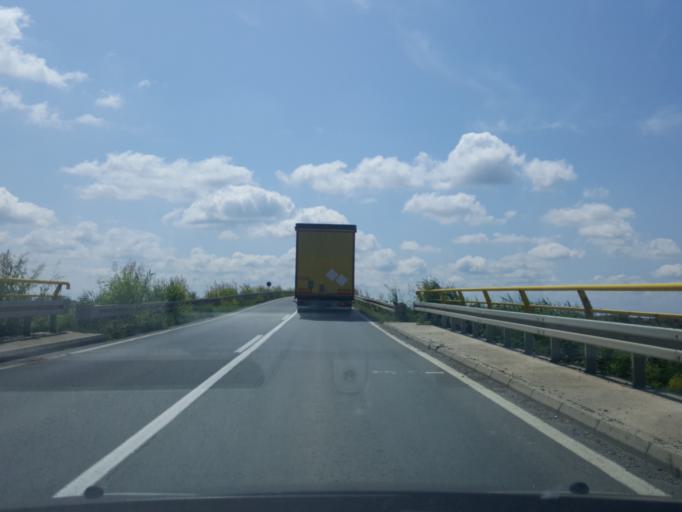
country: RS
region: Autonomna Pokrajina Vojvodina
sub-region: Sremski Okrug
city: Sremska Mitrovica
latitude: 44.9871
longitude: 19.6401
